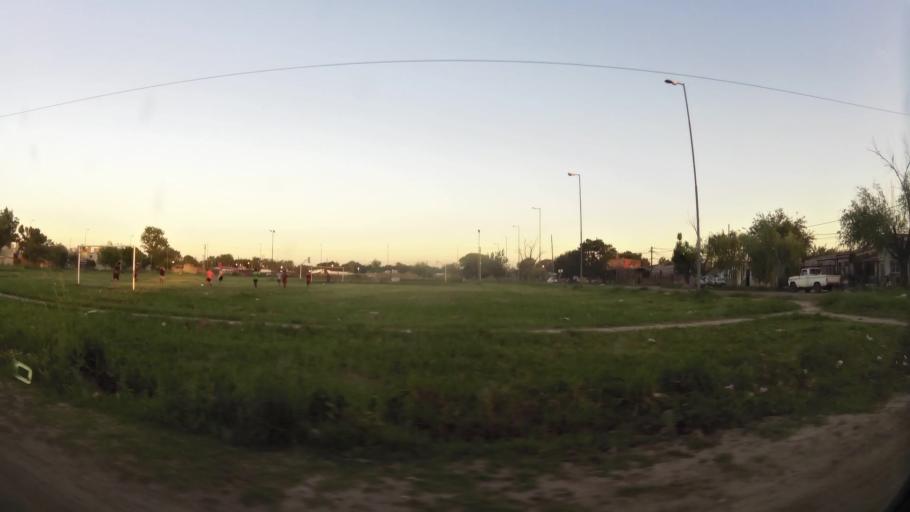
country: AR
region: Santa Fe
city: Santa Fe de la Vera Cruz
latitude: -31.5932
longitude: -60.6966
